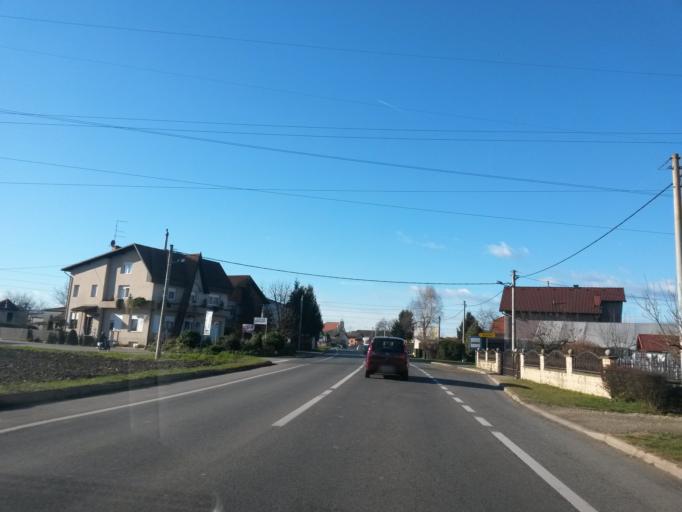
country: HR
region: Varazdinska
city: Nedeljanec
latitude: 46.2913
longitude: 16.3017
